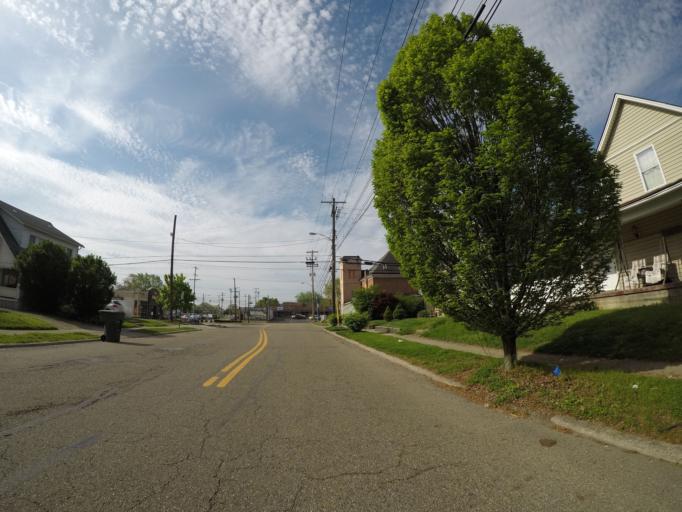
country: US
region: Ohio
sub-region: Franklin County
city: Grandview Heights
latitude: 39.9898
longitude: -83.0491
